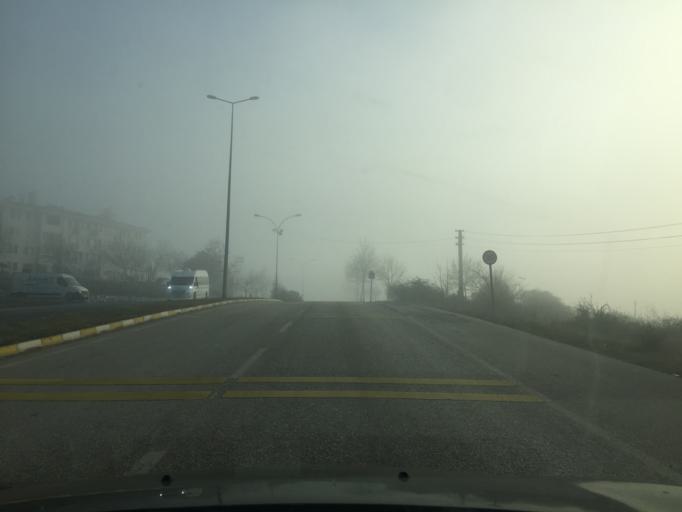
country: TR
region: Duzce
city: Duzce
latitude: 40.8677
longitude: 31.2193
